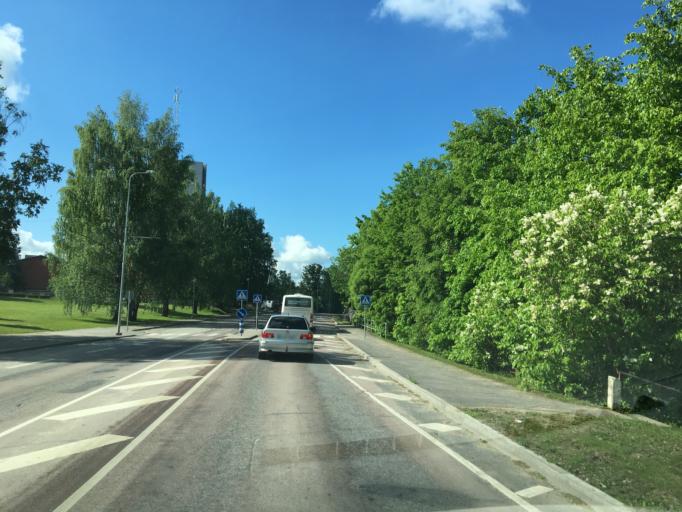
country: EE
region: Tartu
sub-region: Elva linn
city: Elva
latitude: 58.2350
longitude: 26.4108
